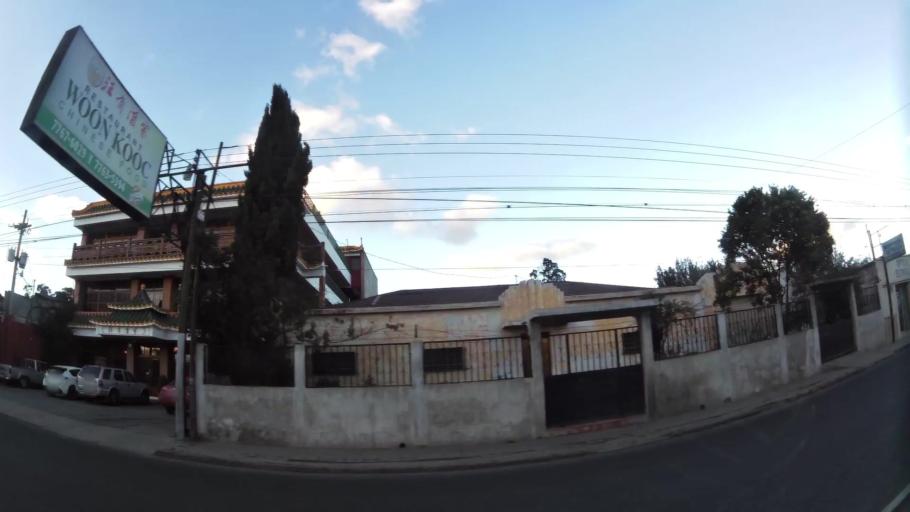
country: GT
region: Quetzaltenango
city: Quetzaltenango
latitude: 14.8437
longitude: -91.5157
